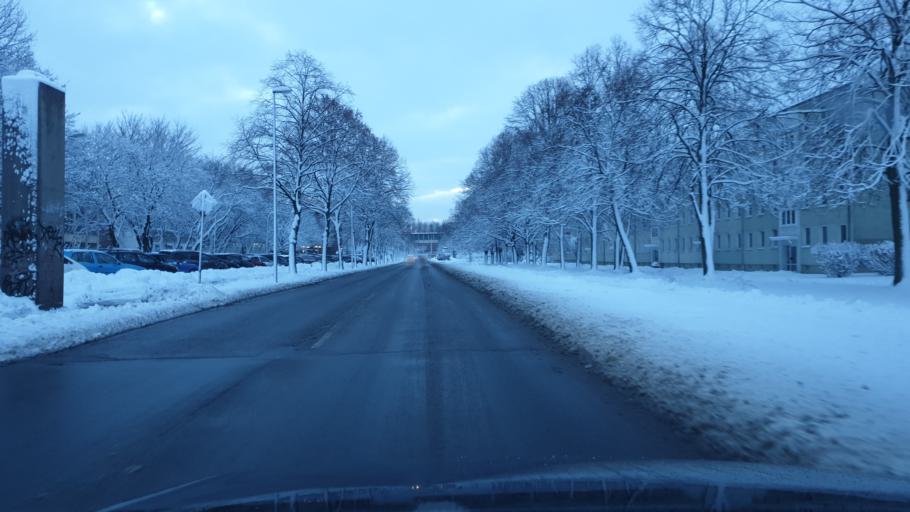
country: DE
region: Saxony
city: Chemnitz
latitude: 50.8562
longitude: 12.9170
